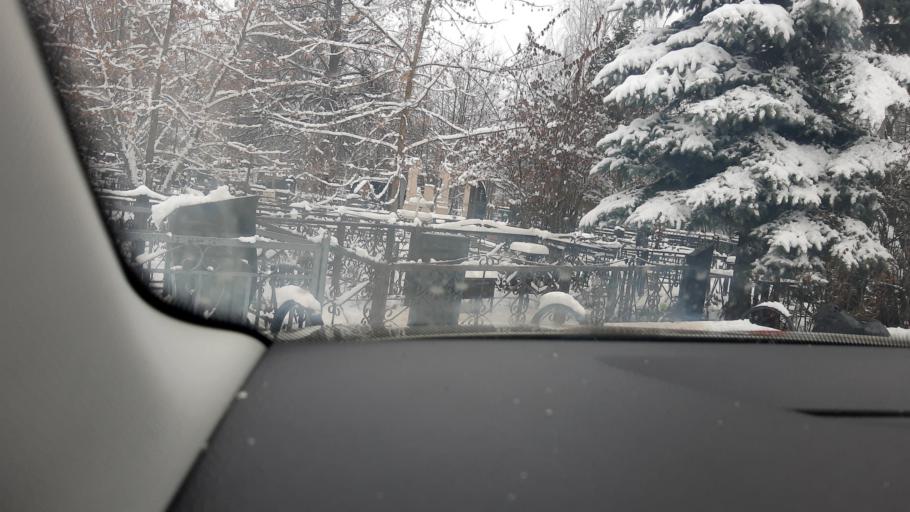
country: RU
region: Moscow
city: Zagor'ye
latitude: 55.5638
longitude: 37.6779
